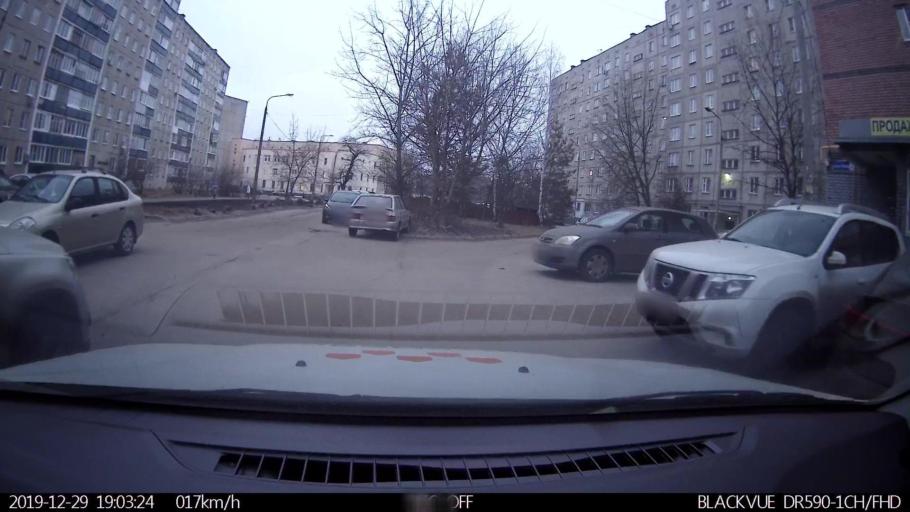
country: RU
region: Nizjnij Novgorod
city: Neklyudovo
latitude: 56.3581
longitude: 43.8558
